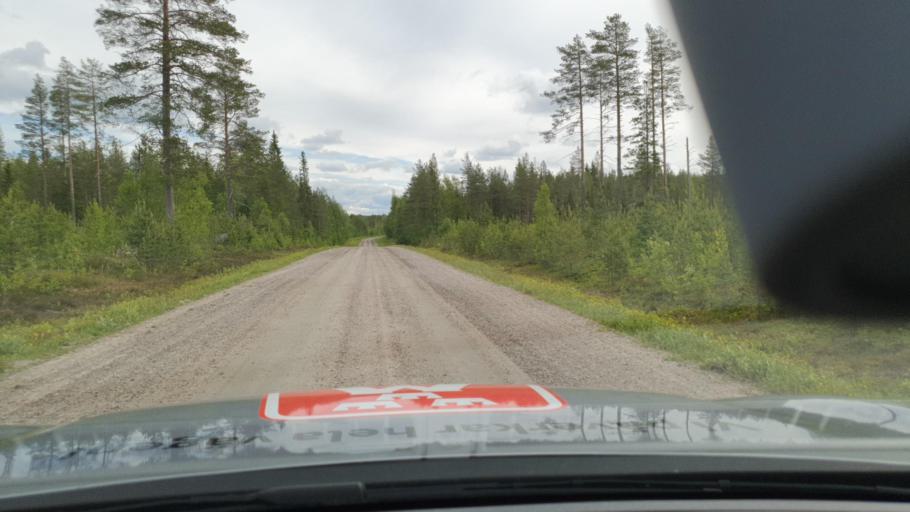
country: FI
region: Lapland
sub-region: Torniolaakso
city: Ylitornio
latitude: 65.9614
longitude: 23.6479
